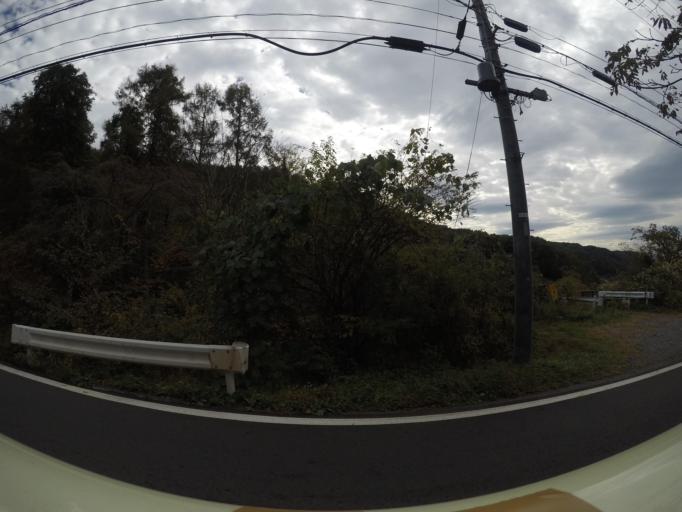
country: JP
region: Nagano
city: Chino
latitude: 35.9542
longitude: 138.1092
